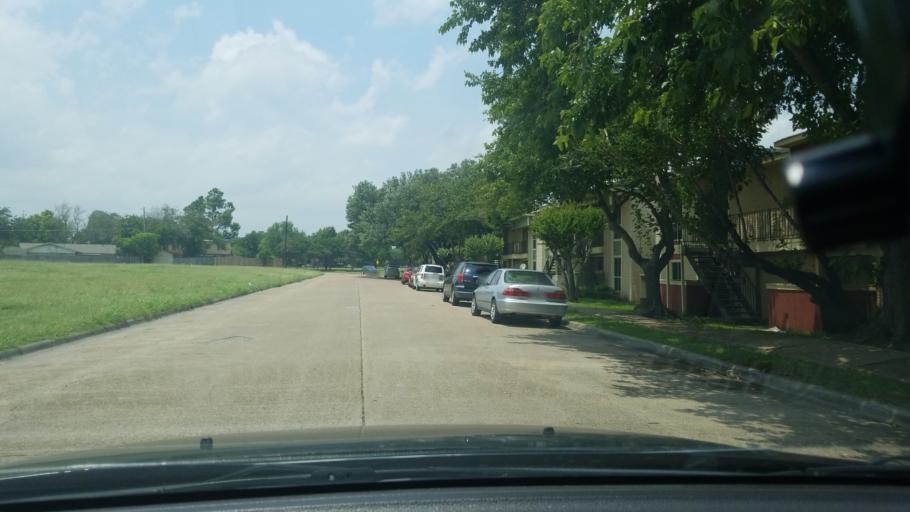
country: US
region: Texas
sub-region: Dallas County
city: Mesquite
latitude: 32.7939
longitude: -96.6441
